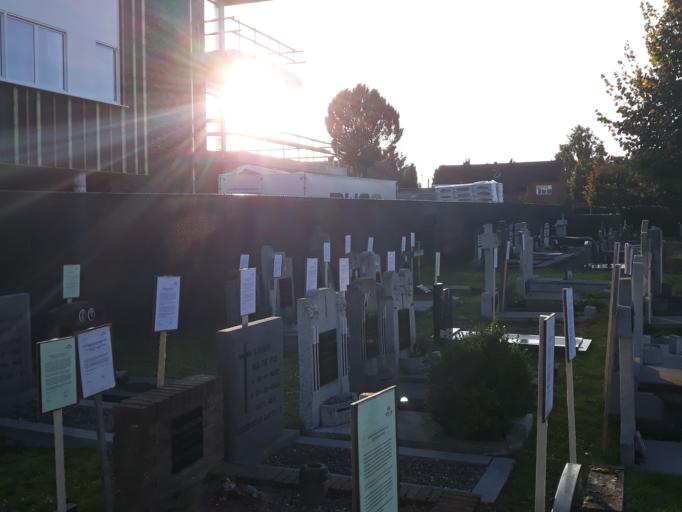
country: BE
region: Flanders
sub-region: Provincie Antwerpen
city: Ravels
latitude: 51.3711
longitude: 4.9955
